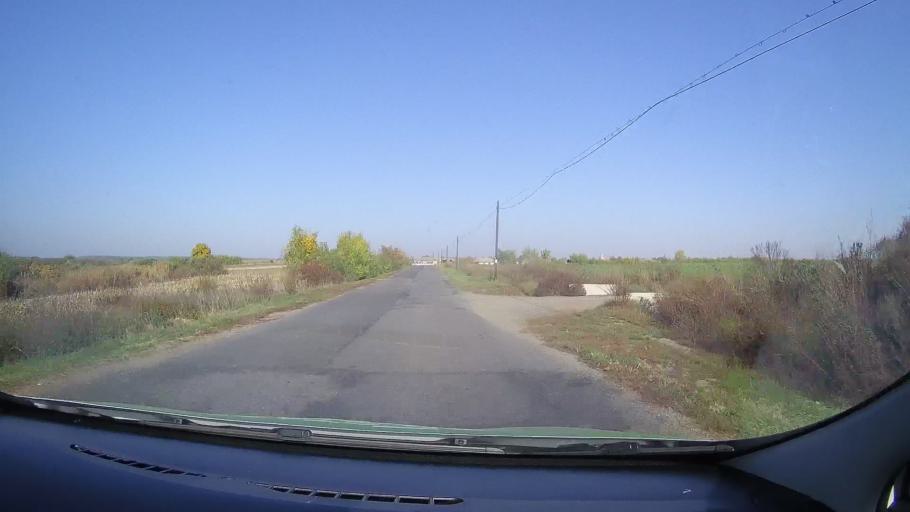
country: RO
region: Satu Mare
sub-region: Comuna Ciumesti
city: Ciumesti
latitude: 47.6505
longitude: 22.3367
